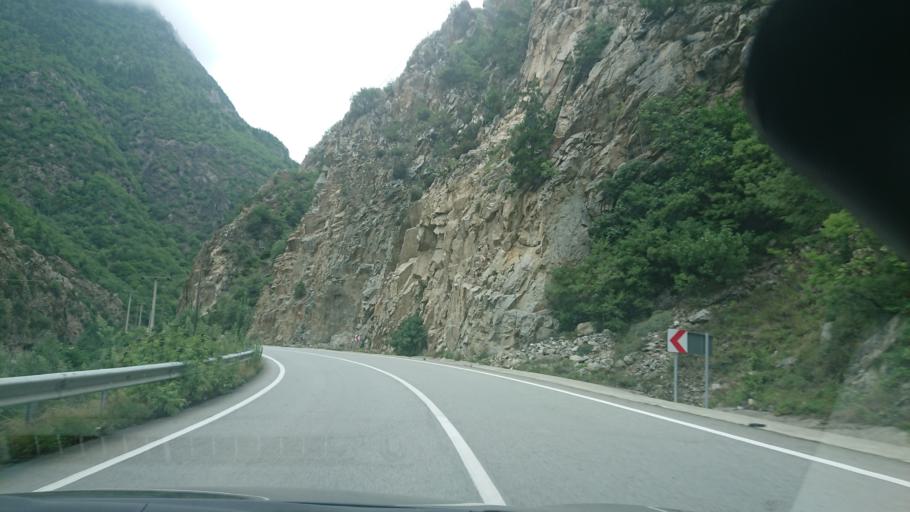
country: TR
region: Gumushane
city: Kurtun
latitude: 40.7270
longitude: 39.0217
